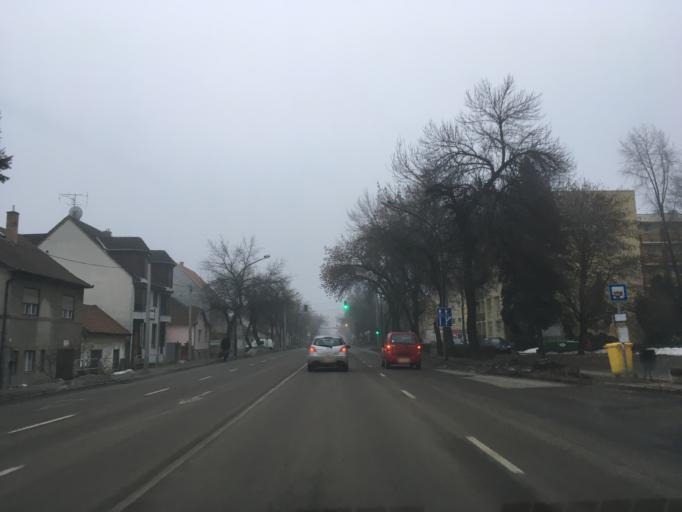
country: HU
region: Heves
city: Eger
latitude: 47.8832
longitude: 20.3813
